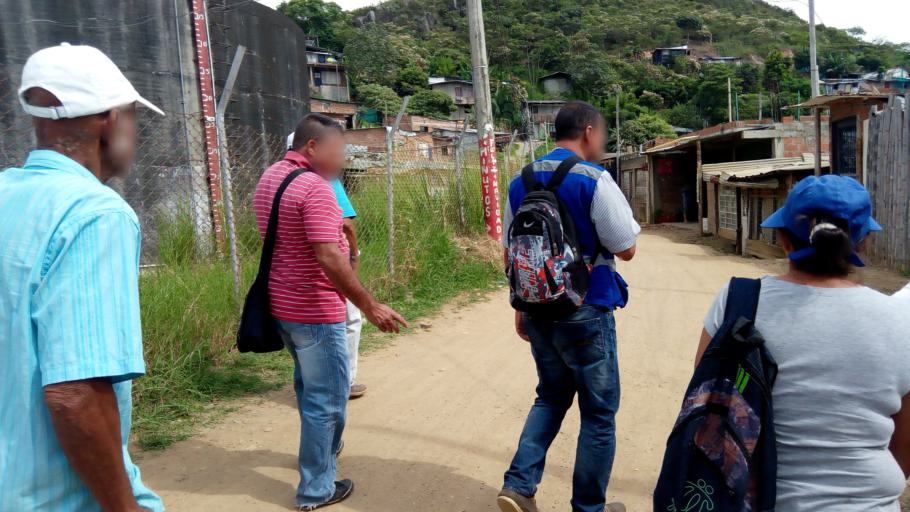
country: CO
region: Valle del Cauca
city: Cali
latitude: 3.3834
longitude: -76.5634
